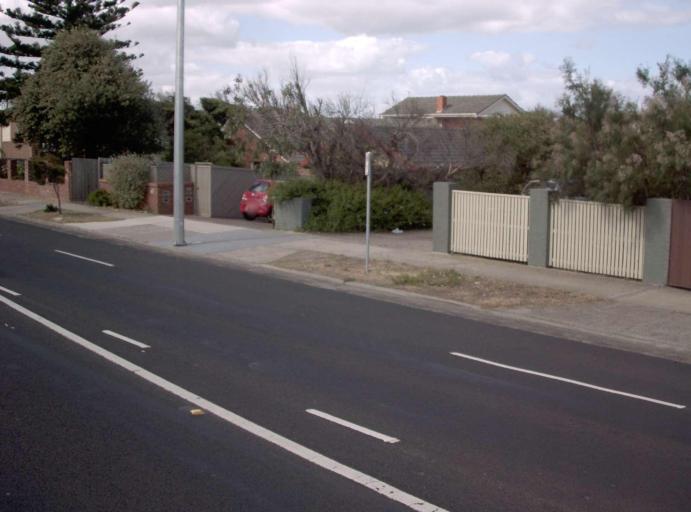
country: AU
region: Victoria
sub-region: Kingston
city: Aspendale
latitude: -38.0283
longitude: 145.1025
